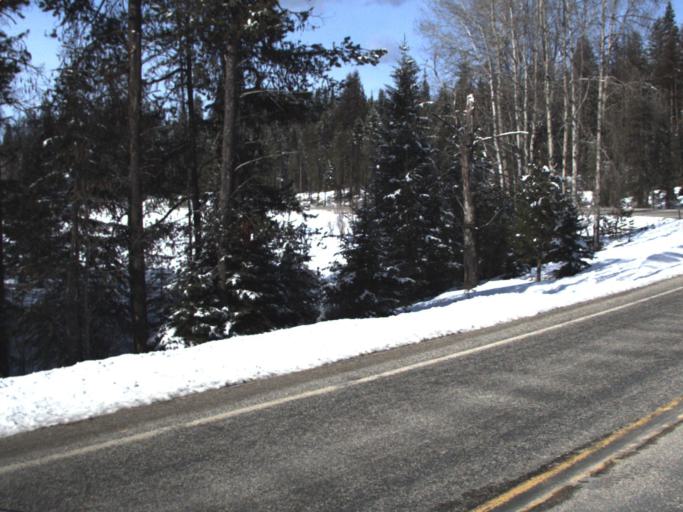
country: CA
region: British Columbia
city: Fruitvale
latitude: 48.6739
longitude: -117.4672
